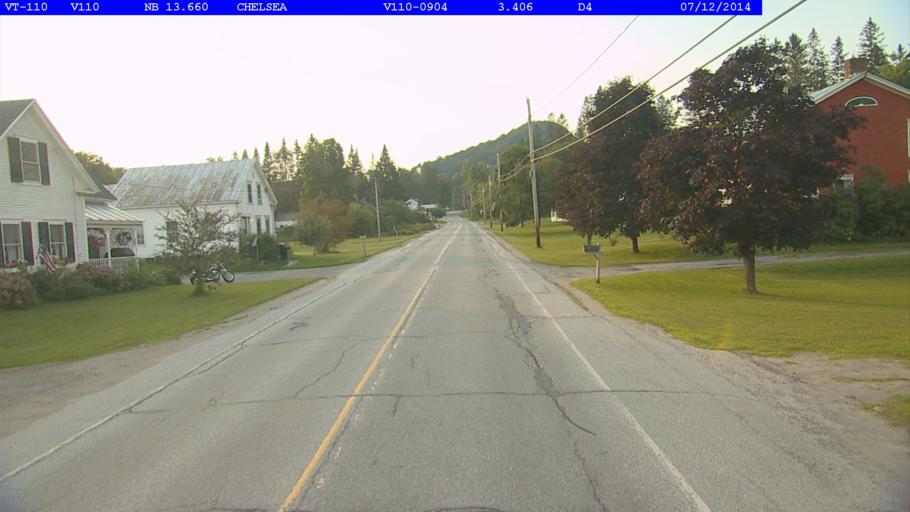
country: US
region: Vermont
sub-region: Orange County
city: Chelsea
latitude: 43.9954
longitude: -72.4477
